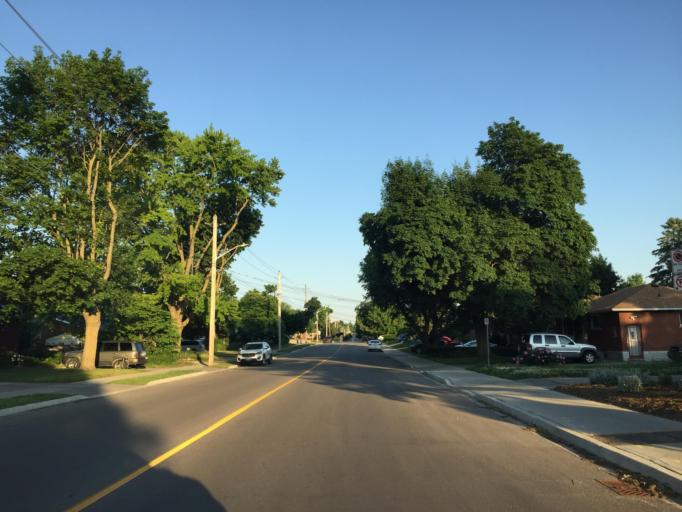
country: CA
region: Ontario
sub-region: Wellington County
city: Guelph
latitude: 43.5620
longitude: -80.2566
